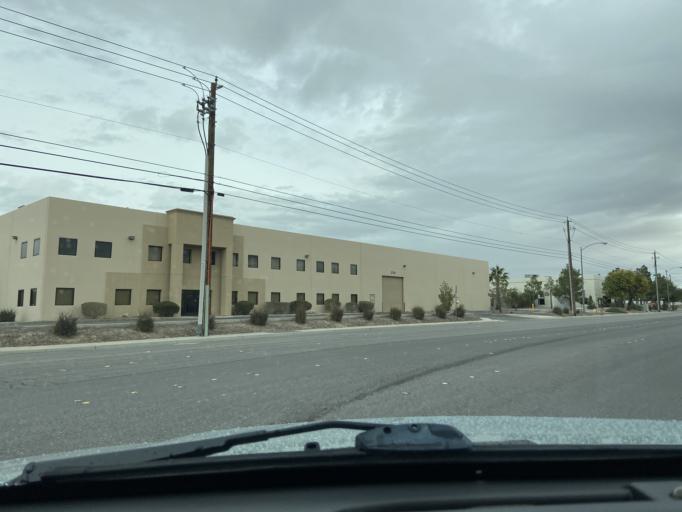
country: US
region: Nevada
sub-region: Clark County
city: North Las Vegas
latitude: 36.2469
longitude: -115.1123
